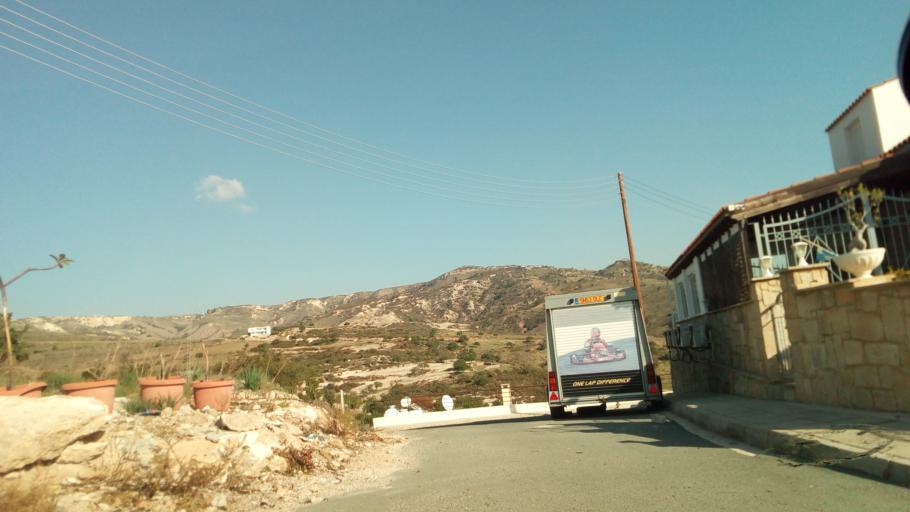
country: CY
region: Pafos
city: Pegeia
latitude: 34.8852
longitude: 32.3889
